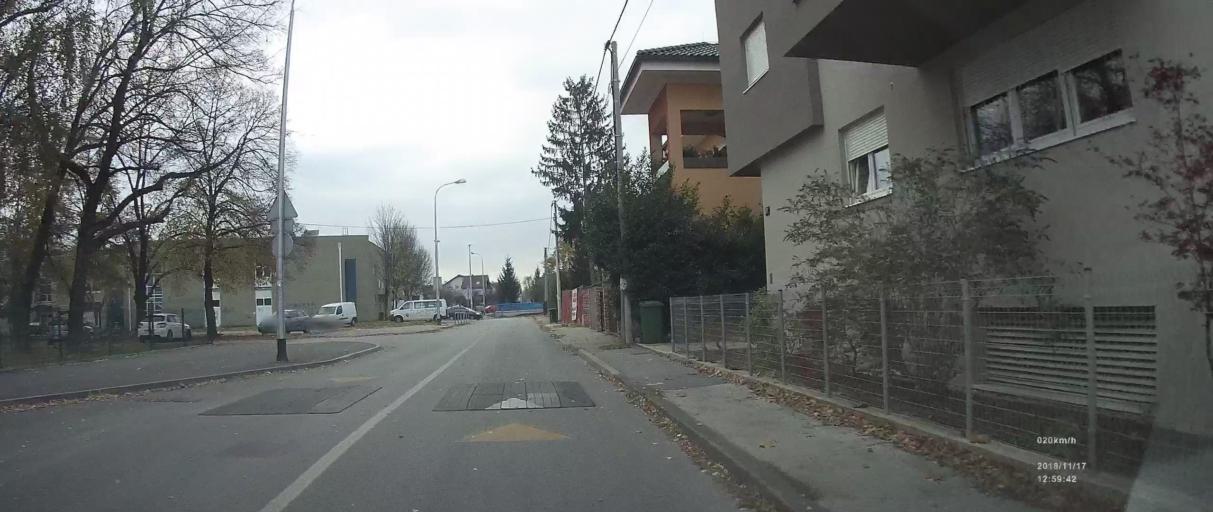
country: HR
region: Grad Zagreb
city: Jankomir
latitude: 45.7941
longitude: 15.9042
